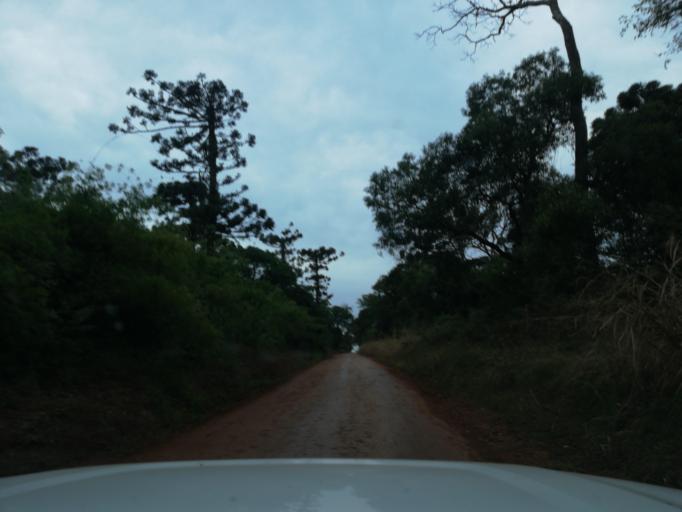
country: AR
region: Misiones
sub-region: Departamento de San Pedro
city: San Pedro
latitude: -26.6303
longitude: -54.1001
